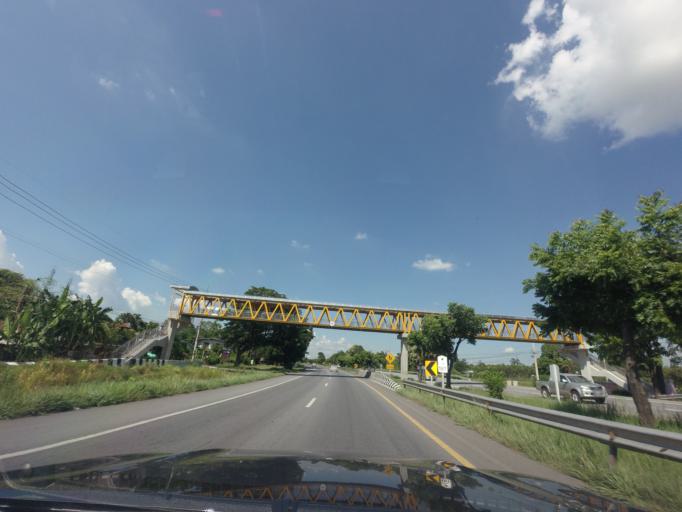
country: TH
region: Nakhon Ratchasima
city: Non Sung
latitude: 15.1476
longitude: 102.3248
